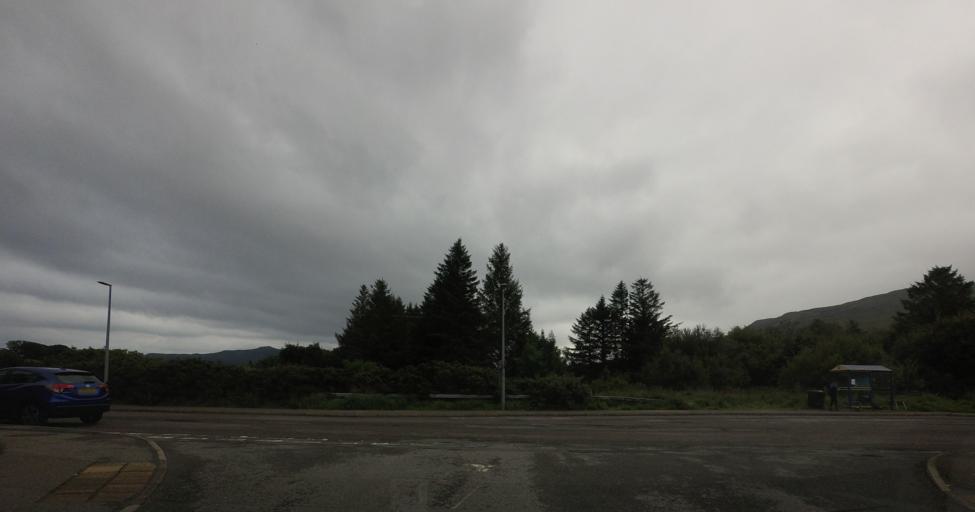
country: GB
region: Scotland
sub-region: Highland
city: Portree
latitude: 57.4175
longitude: -6.2082
